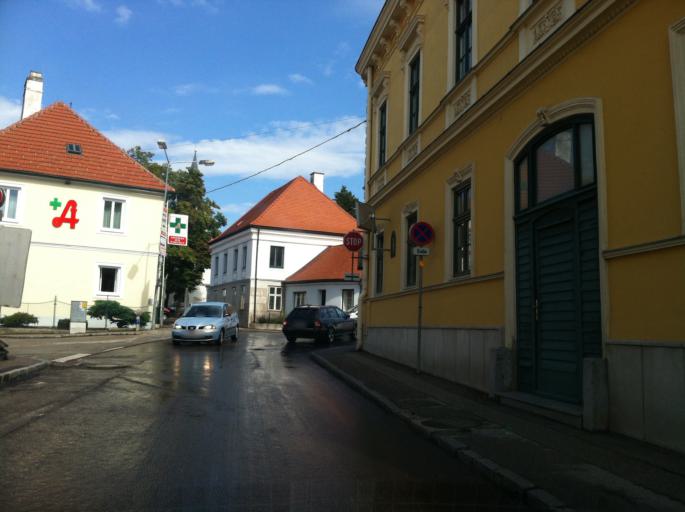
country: AT
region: Lower Austria
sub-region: Politischer Bezirk Tulln
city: Sieghartskirchen
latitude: 48.2547
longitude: 16.0133
